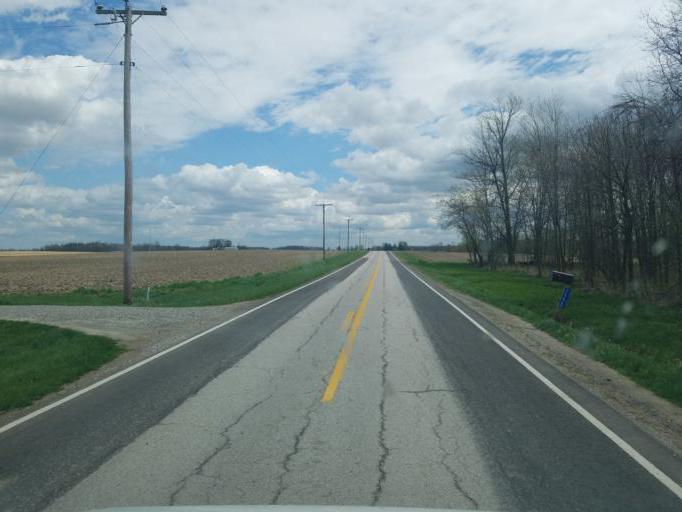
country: US
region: Ohio
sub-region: Crawford County
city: Bucyrus
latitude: 40.8634
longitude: -82.9907
